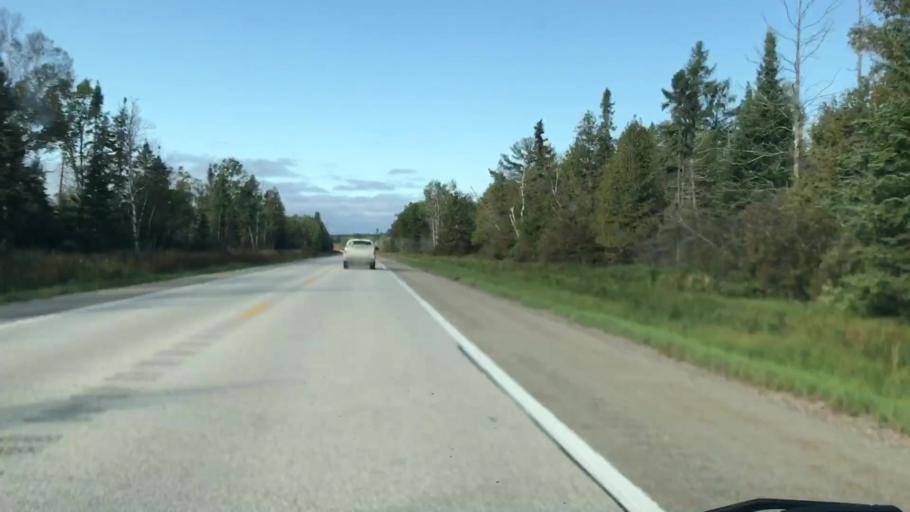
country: US
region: Michigan
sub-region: Luce County
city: Newberry
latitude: 46.3206
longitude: -85.1856
